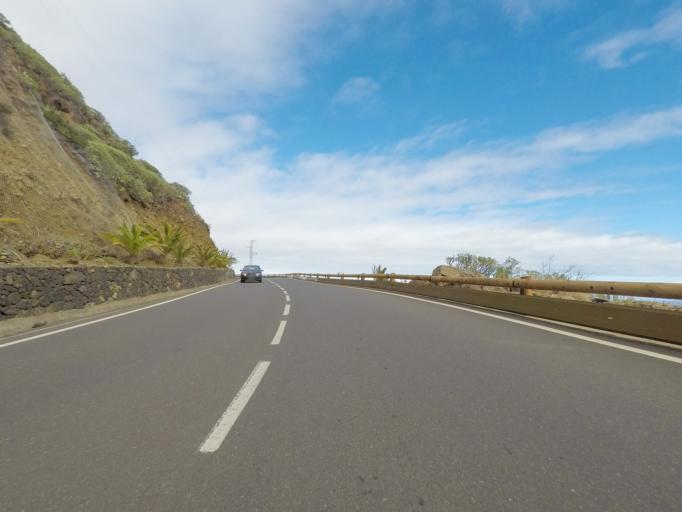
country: ES
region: Canary Islands
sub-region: Provincia de Santa Cruz de Tenerife
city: Agulo
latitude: 28.1839
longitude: -17.1876
